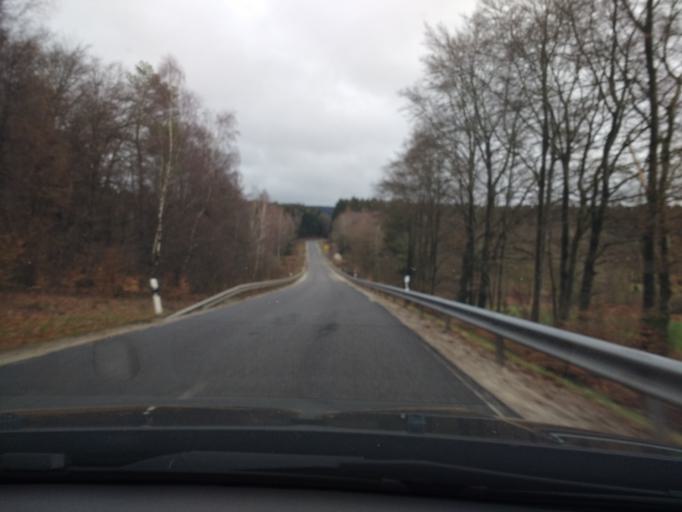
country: DE
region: Rheinland-Pfalz
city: Damflos
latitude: 49.6807
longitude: 6.9681
